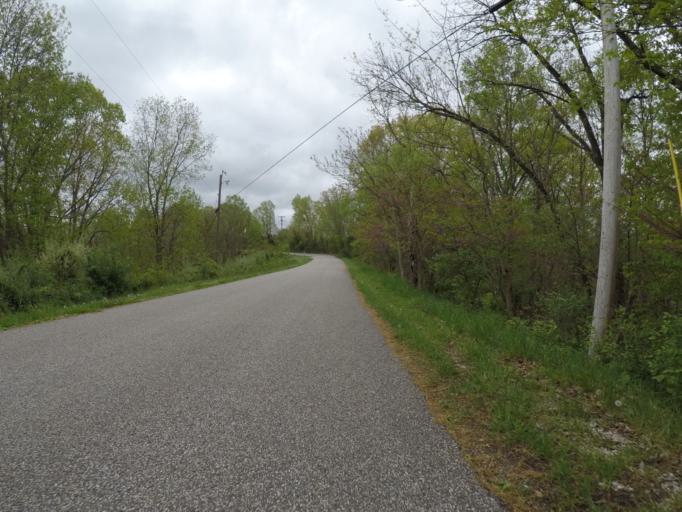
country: US
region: West Virginia
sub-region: Cabell County
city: Barboursville
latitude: 38.4033
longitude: -82.2698
